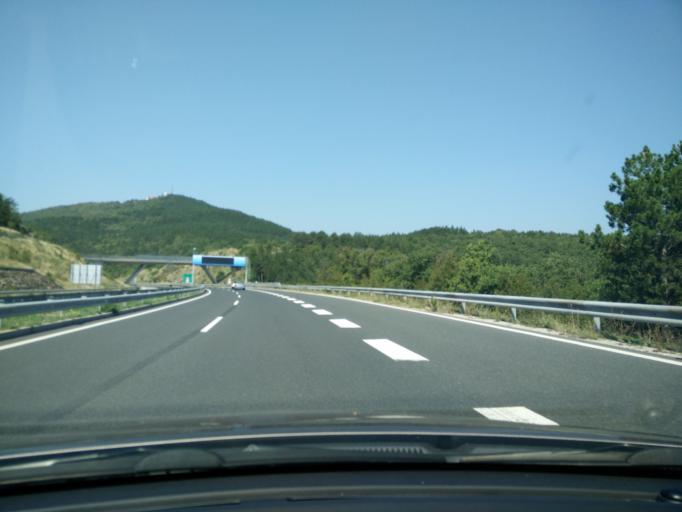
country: SI
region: Koper-Capodistria
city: Sv. Anton
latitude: 45.5553
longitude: 13.8534
